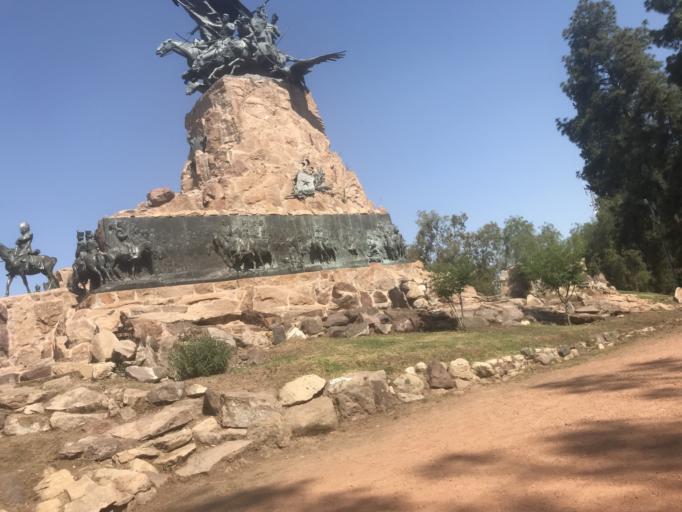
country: AR
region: Mendoza
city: Mendoza
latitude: -32.8886
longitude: -68.8915
